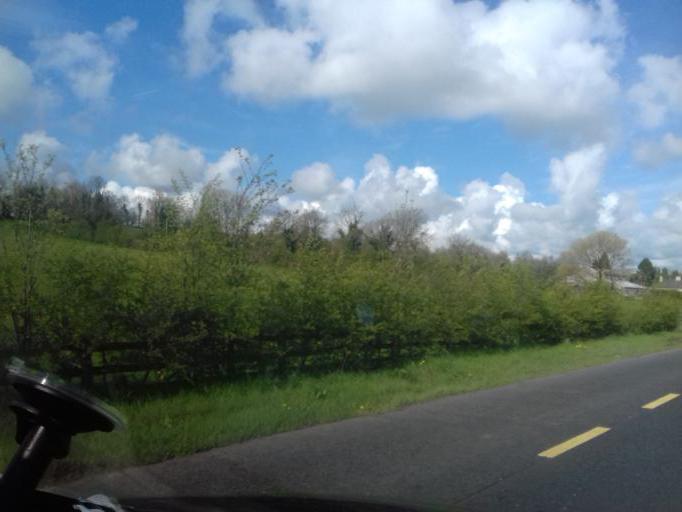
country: IE
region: Ulster
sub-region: An Cabhan
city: Cavan
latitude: 53.9892
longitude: -7.2621
